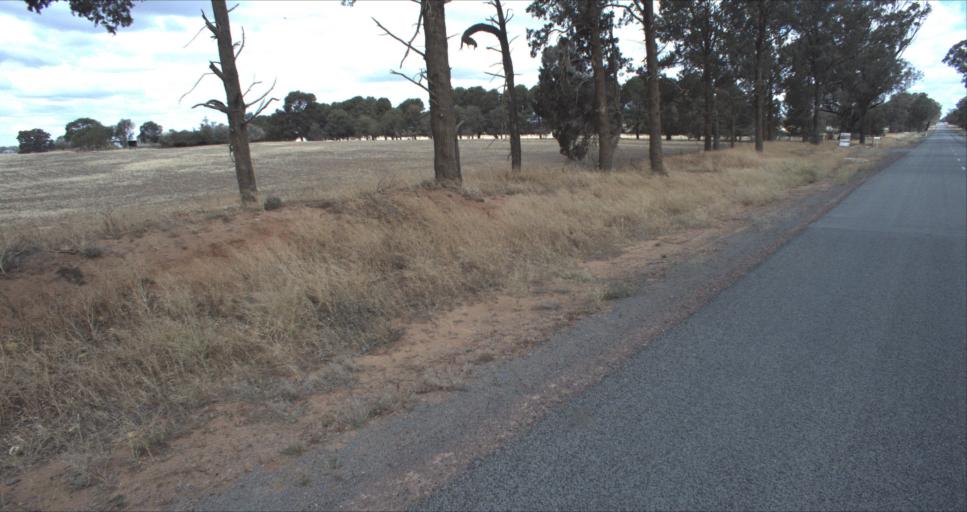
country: AU
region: New South Wales
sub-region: Leeton
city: Leeton
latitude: -34.6600
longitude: 146.3495
